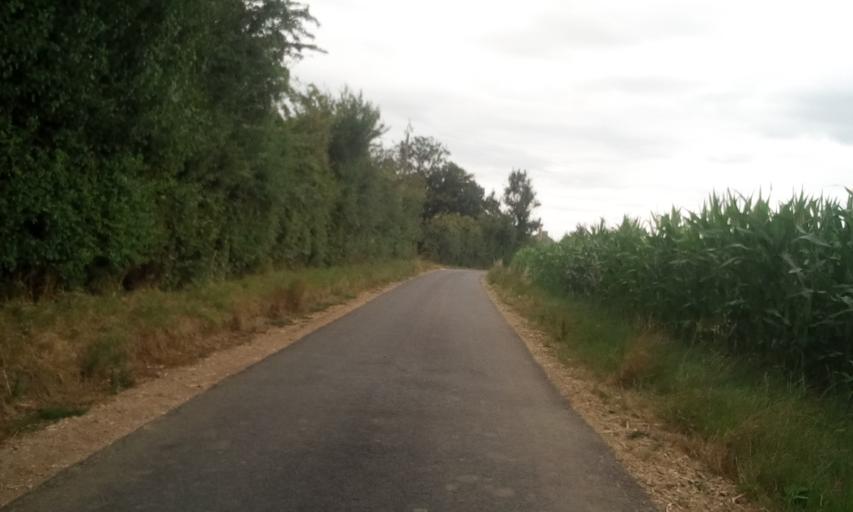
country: FR
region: Lower Normandy
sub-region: Departement du Calvados
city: Thury-Harcourt
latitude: 49.0014
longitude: -0.4417
